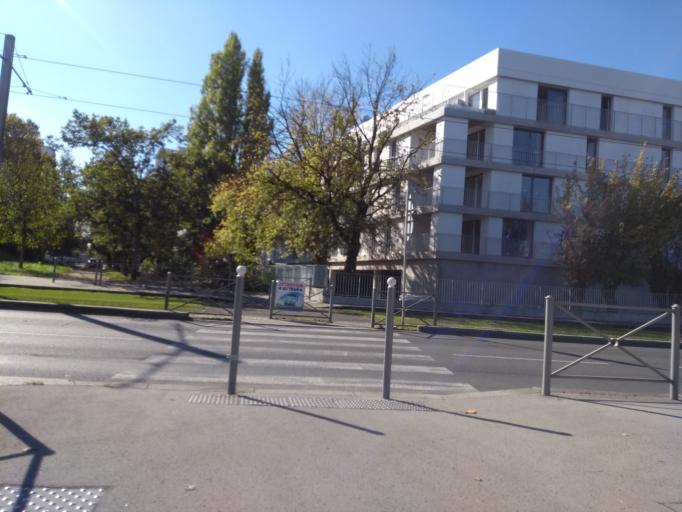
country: FR
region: Aquitaine
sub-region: Departement de la Gironde
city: Pessac
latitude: 44.7942
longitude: -0.6294
